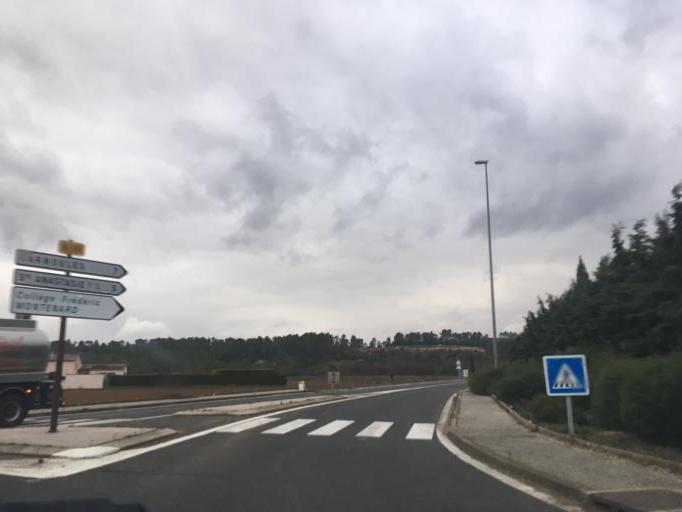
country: FR
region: Provence-Alpes-Cote d'Azur
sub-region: Departement du Var
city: Besse-sur-Issole
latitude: 43.3483
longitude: 6.1816
